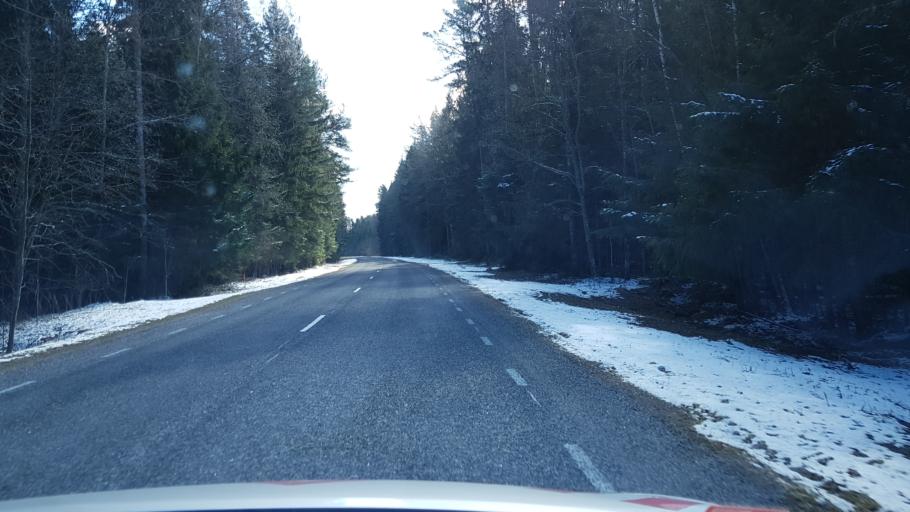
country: EE
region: Harju
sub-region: Loksa linn
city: Loksa
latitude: 59.5673
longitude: 25.9405
